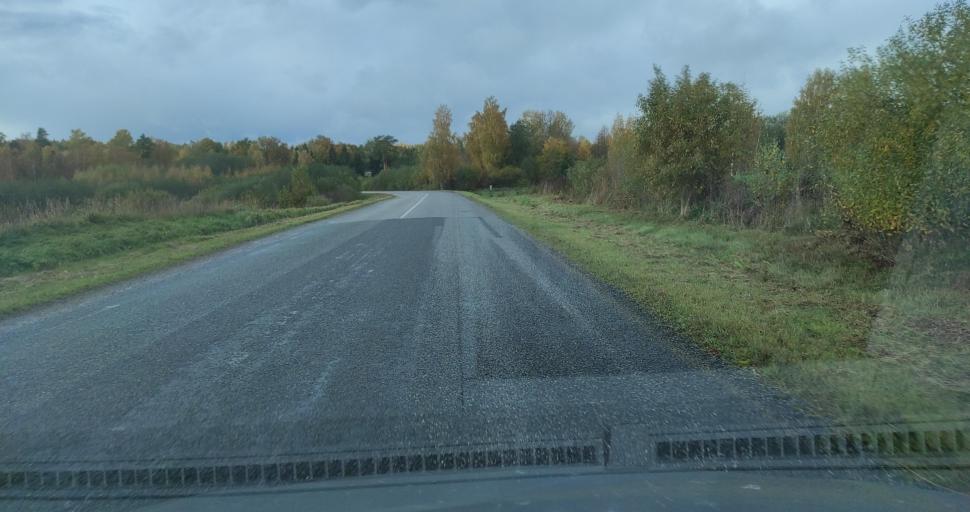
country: LV
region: Skrunda
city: Skrunda
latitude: 56.5994
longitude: 21.9062
